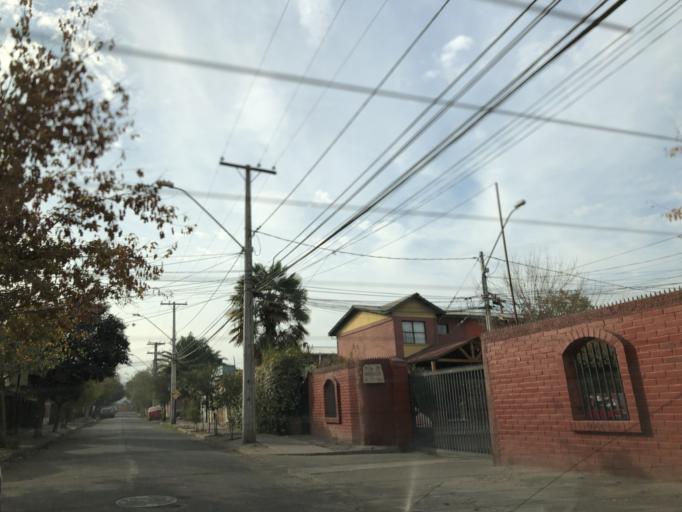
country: CL
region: Santiago Metropolitan
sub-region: Provincia de Cordillera
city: Puente Alto
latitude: -33.5844
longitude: -70.5524
